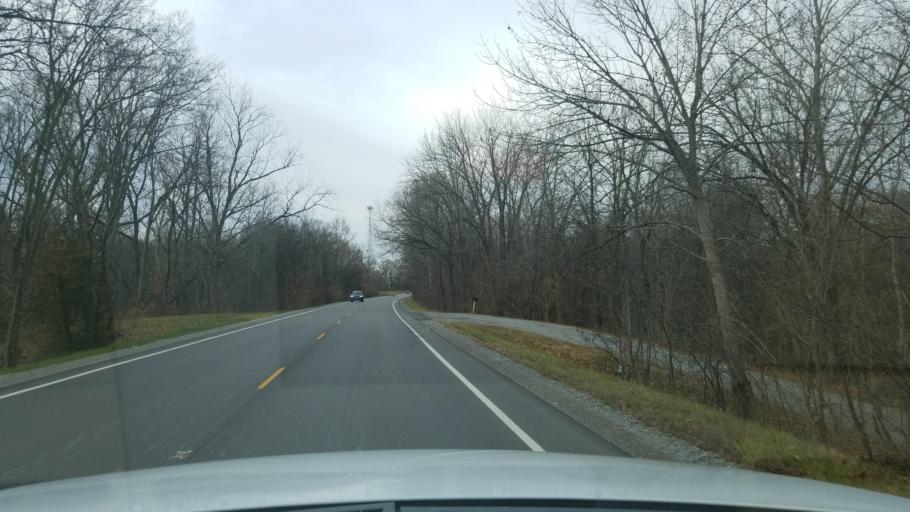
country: US
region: Illinois
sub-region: White County
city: Carmi
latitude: 37.9110
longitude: -88.1310
